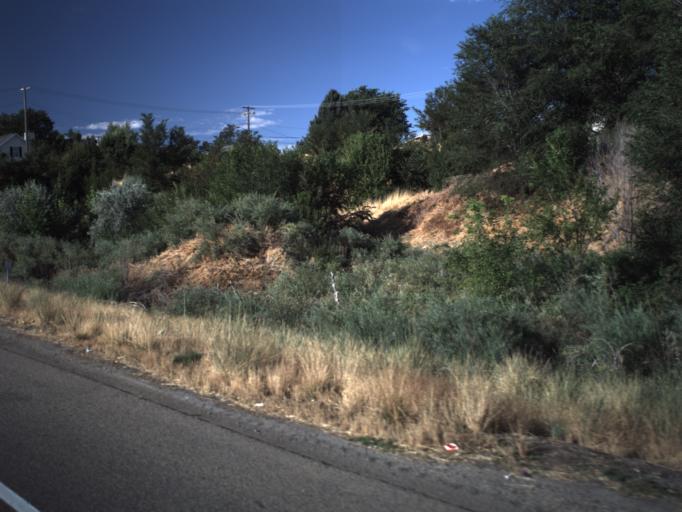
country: US
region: Utah
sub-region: Utah County
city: Spanish Fork
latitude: 40.0889
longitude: -111.6559
